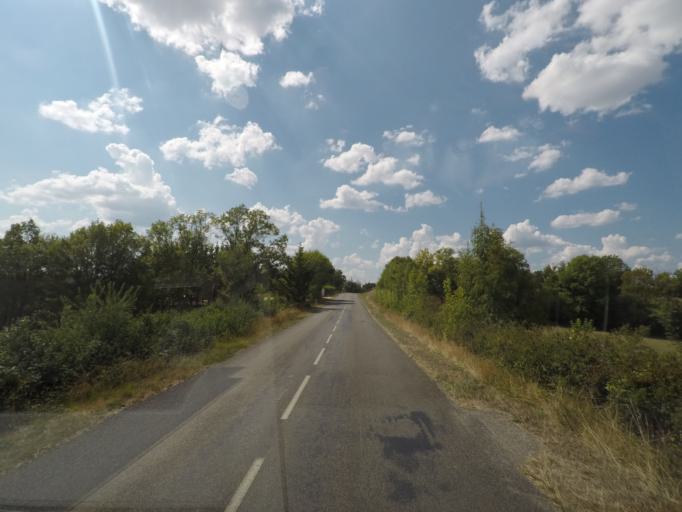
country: FR
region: Midi-Pyrenees
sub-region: Departement du Lot
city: Le Vigan
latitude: 44.6427
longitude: 1.5779
